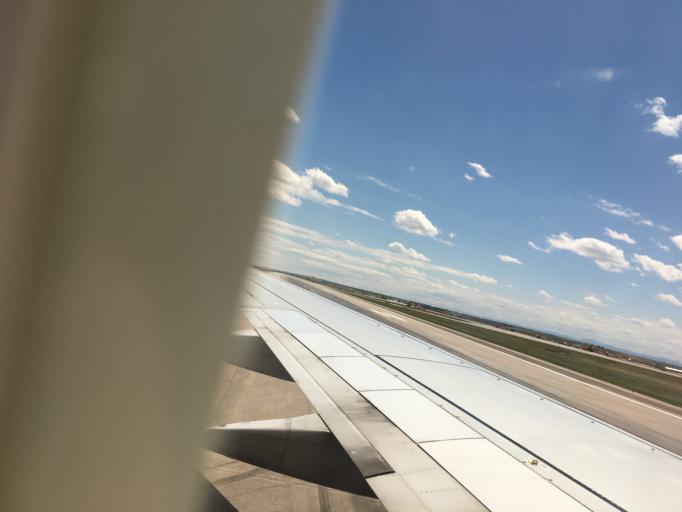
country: US
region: Colorado
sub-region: Weld County
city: Lochbuie
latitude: 39.8568
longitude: -104.6600
